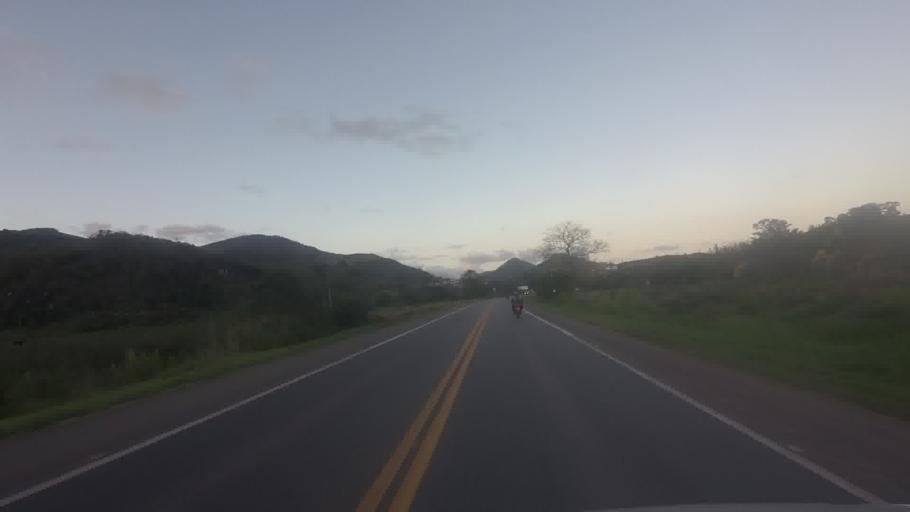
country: BR
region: Espirito Santo
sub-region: Rio Novo Do Sul
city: Rio Novo do Sul
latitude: -20.8743
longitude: -40.9517
